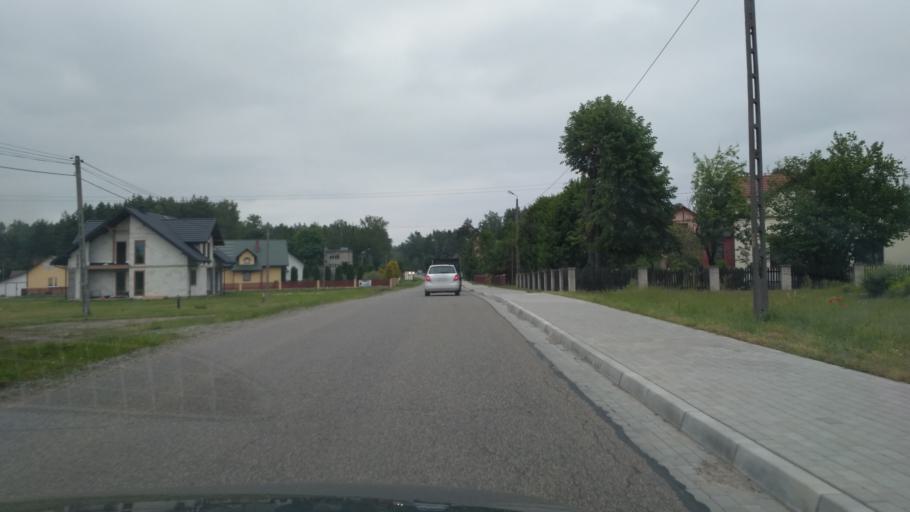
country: PL
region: Subcarpathian Voivodeship
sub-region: Powiat ropczycko-sedziszowski
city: Sedziszow Malopolski
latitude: 50.1400
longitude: 21.6697
